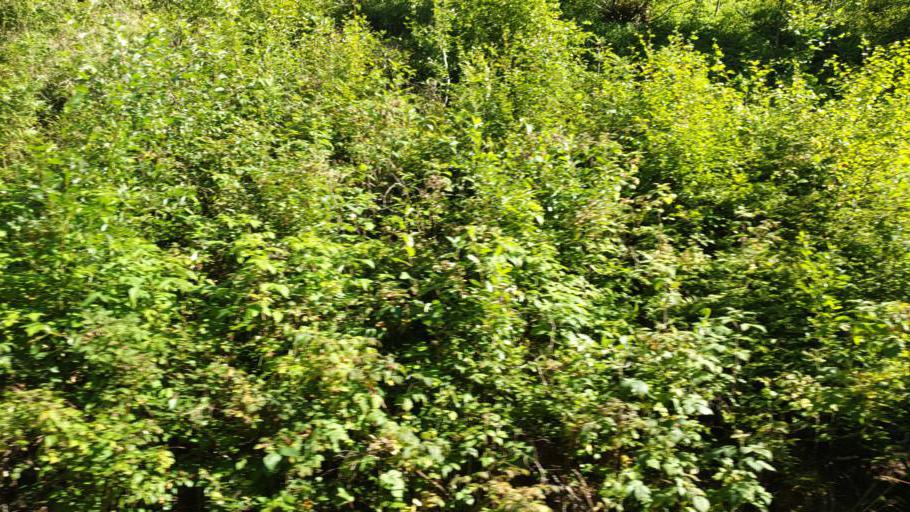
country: NO
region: Sor-Trondelag
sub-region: Meldal
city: Meldal
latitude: 63.1754
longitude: 9.7518
